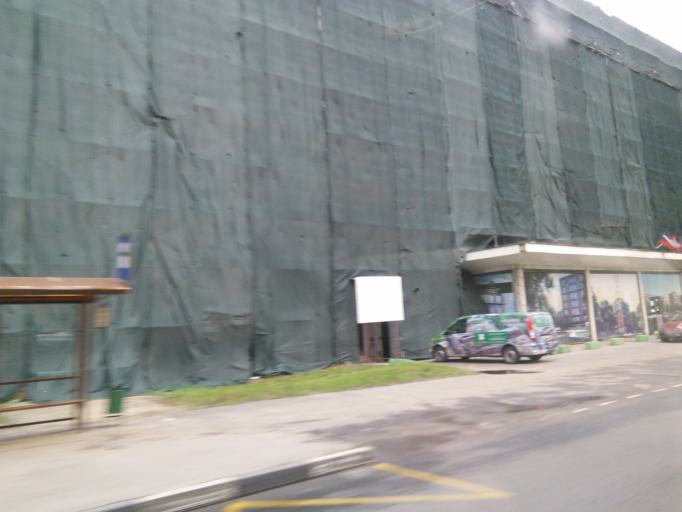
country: RU
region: Moskovskaya
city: Koptevo
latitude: 55.8391
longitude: 37.5159
